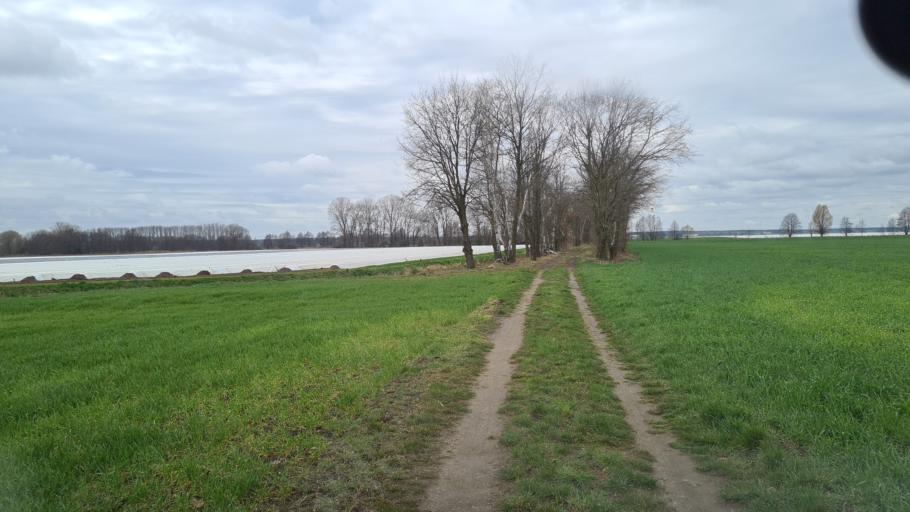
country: DE
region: Brandenburg
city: Doberlug-Kirchhain
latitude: 51.6549
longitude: 13.5695
